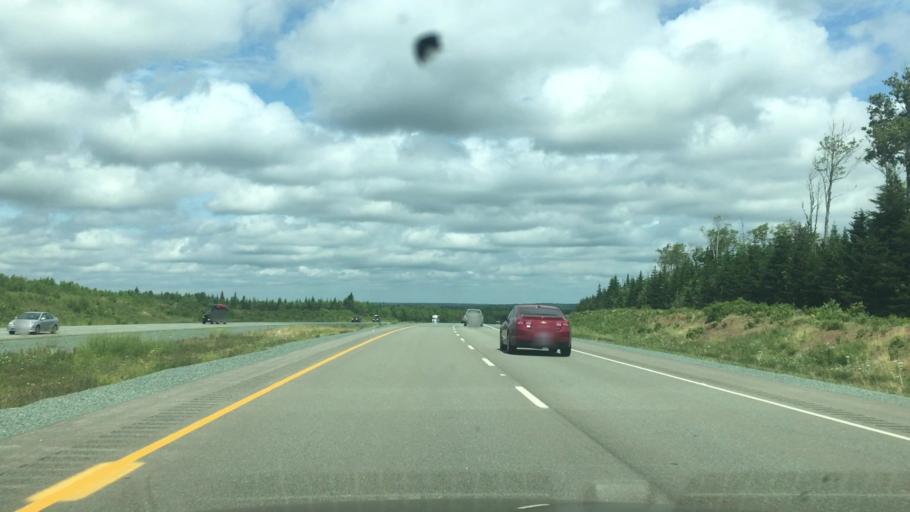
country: CA
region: Nova Scotia
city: Oxford
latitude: 45.6236
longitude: -63.7431
